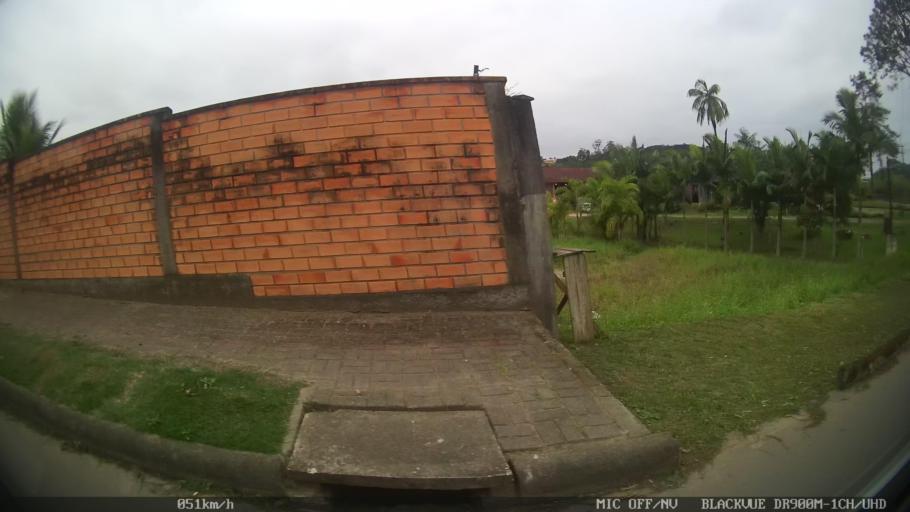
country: BR
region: Santa Catarina
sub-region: Joinville
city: Joinville
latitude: -26.3698
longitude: -48.8460
